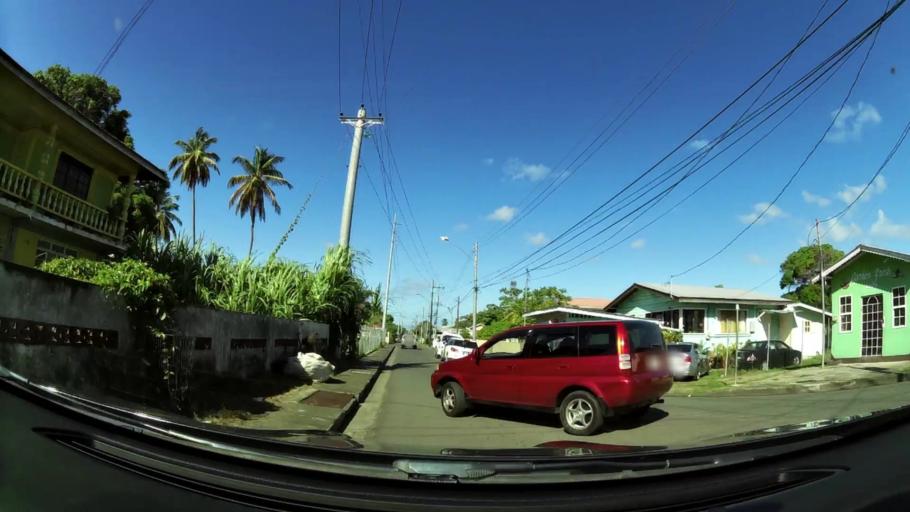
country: TT
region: Tobago
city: Scarborough
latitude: 11.1592
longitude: -60.8083
